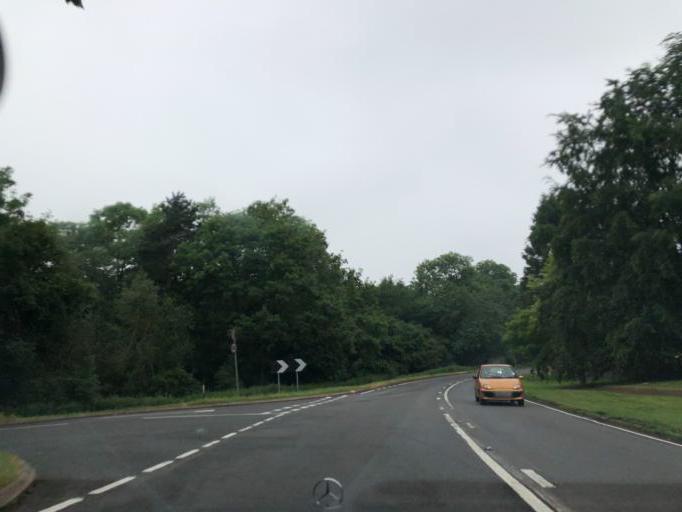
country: GB
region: England
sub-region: Warwickshire
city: Warwick
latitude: 52.2632
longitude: -1.5718
